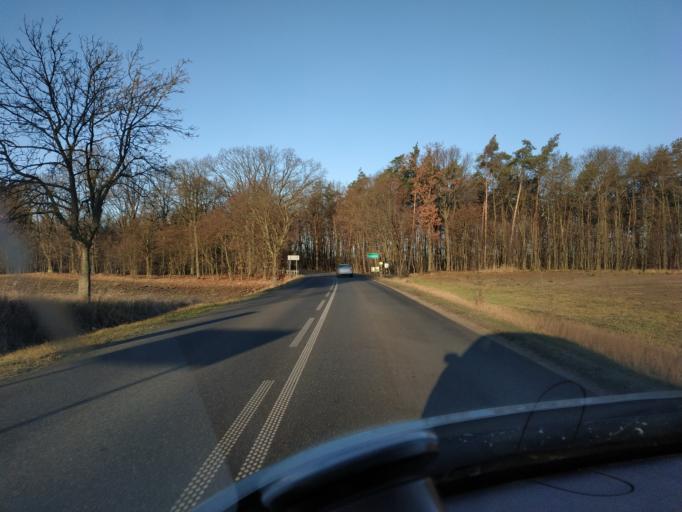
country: PL
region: Kujawsko-Pomorskie
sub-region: Powiat wabrzeski
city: Wabrzezno
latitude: 53.2346
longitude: 18.9502
